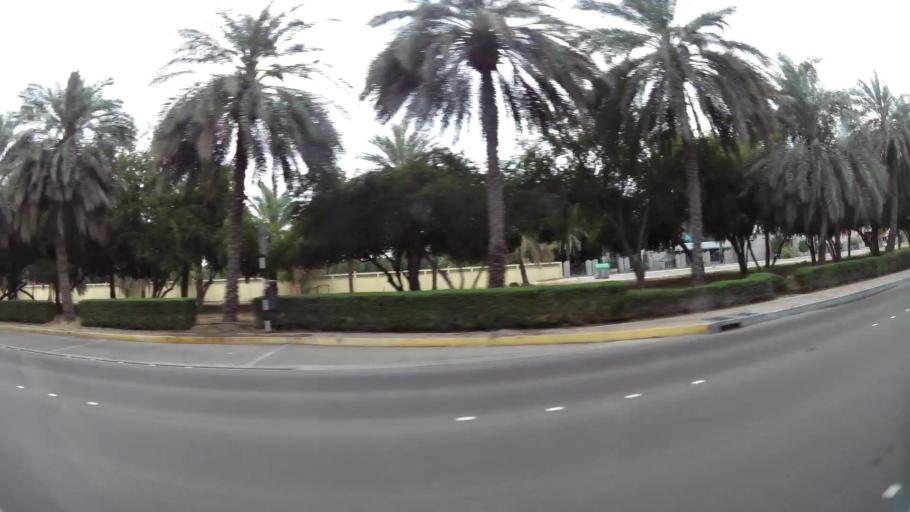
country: AE
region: Abu Dhabi
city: Abu Dhabi
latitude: 24.4408
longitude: 54.3850
